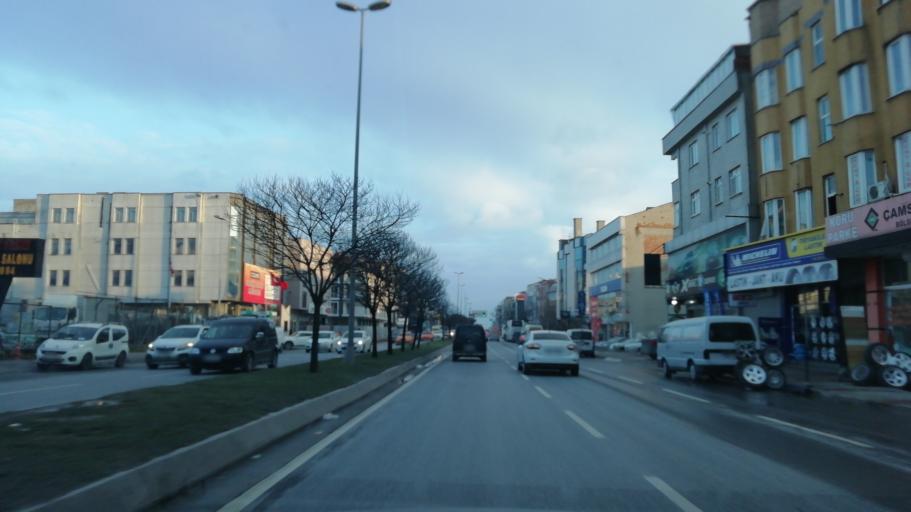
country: TR
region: Istanbul
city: Esenyurt
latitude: 41.0088
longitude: 28.7026
